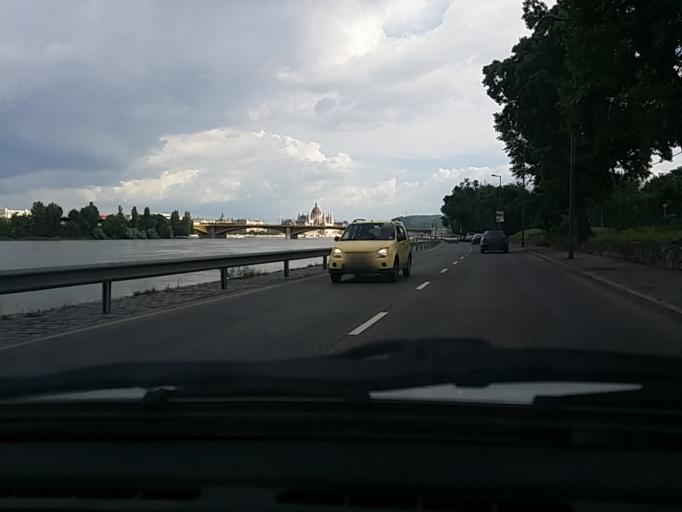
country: HU
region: Budapest
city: Budapest II. keruelet
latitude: 47.5208
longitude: 19.0387
